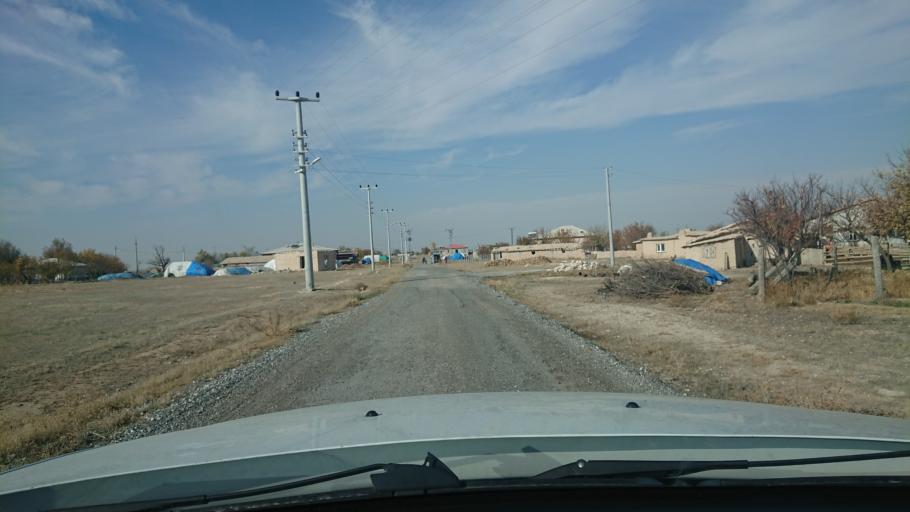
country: TR
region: Aksaray
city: Sultanhani
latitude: 38.2542
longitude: 33.4807
